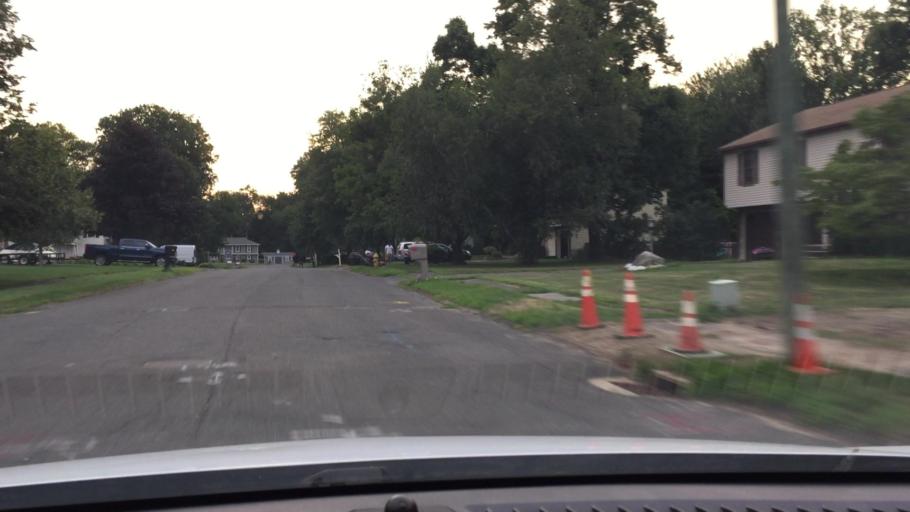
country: US
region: Massachusetts
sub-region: Hampden County
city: Agawam
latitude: 42.0590
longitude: -72.6844
